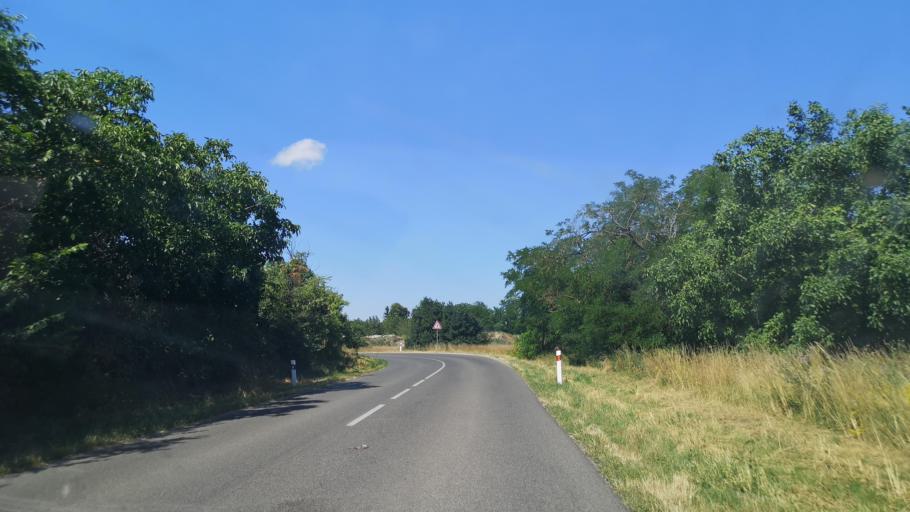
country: SK
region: Trnavsky
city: Dunajska Streda
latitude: 48.0591
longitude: 17.4672
